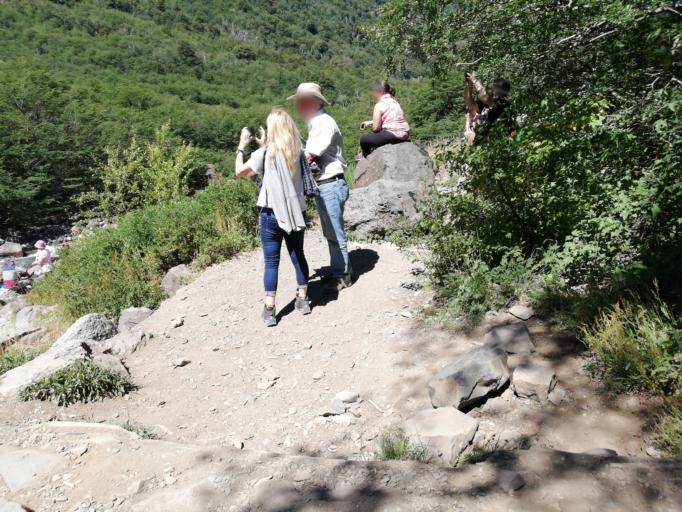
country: AR
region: Neuquen
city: Villa La Angostura
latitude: -41.1910
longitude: -71.8351
